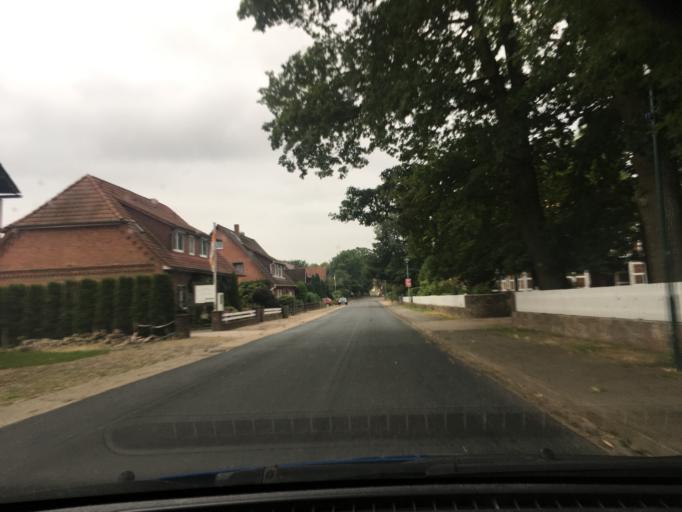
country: DE
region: Lower Saxony
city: Egestorf
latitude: 53.1969
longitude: 10.0644
